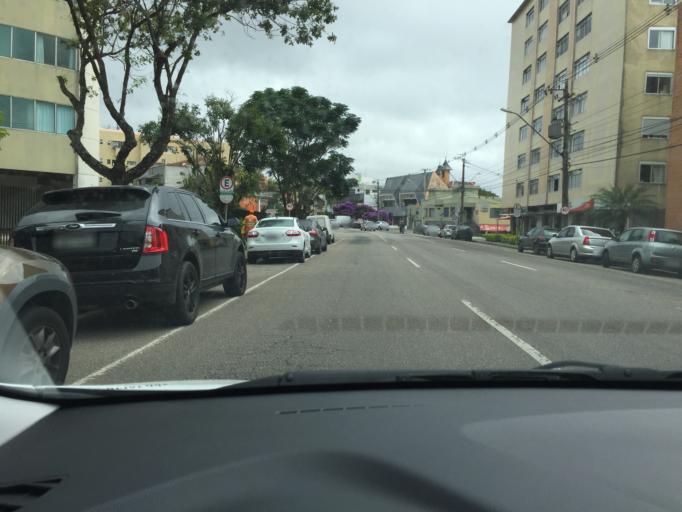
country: BR
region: Parana
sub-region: Curitiba
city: Curitiba
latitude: -25.4223
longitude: -49.2856
